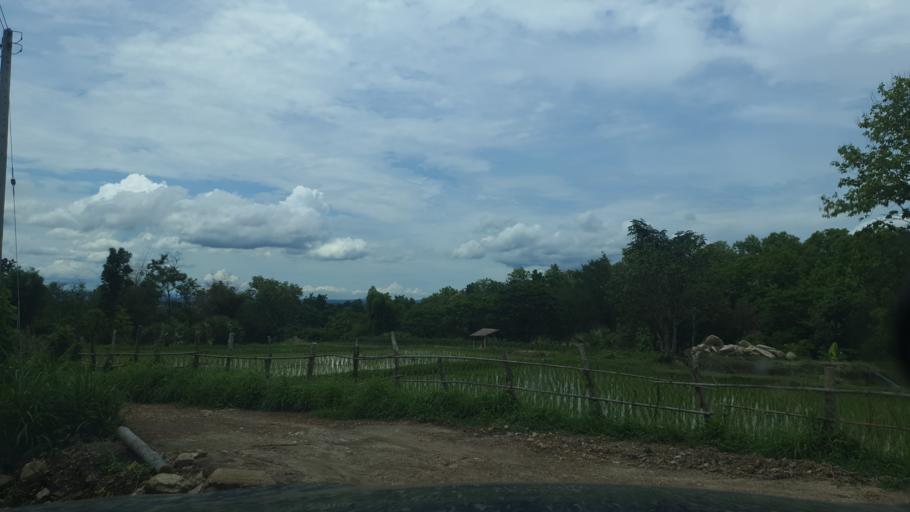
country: TH
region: Lampang
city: Sop Prap
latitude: 17.8569
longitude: 99.3960
